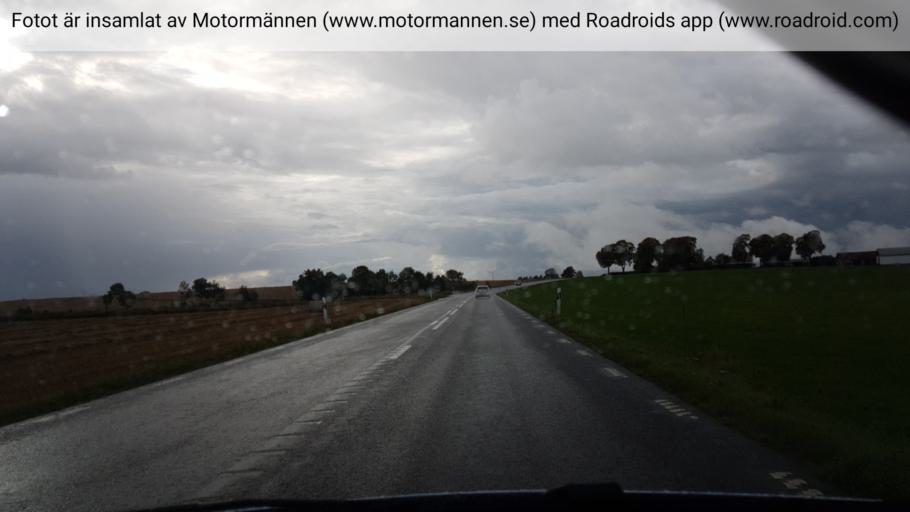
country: SE
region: Vaestra Goetaland
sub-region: Falkopings Kommun
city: Akarp
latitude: 58.0843
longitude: 13.7594
